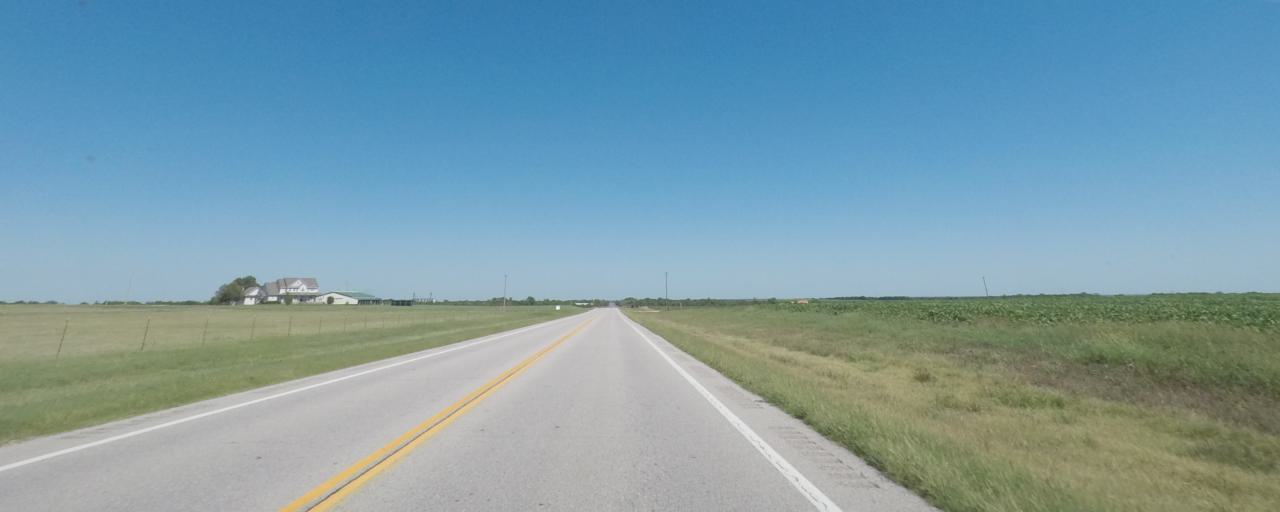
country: US
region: Kansas
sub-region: Sumner County
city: Wellington
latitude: 37.3601
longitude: -97.3850
